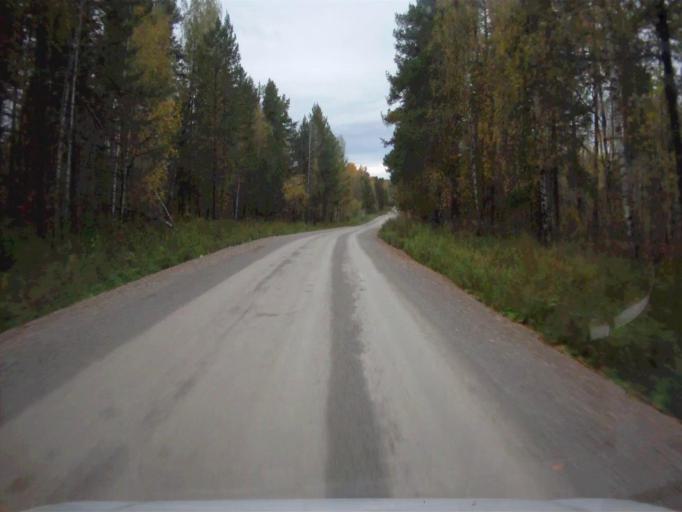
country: RU
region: Chelyabinsk
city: Nyazepetrovsk
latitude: 56.0718
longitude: 59.4297
